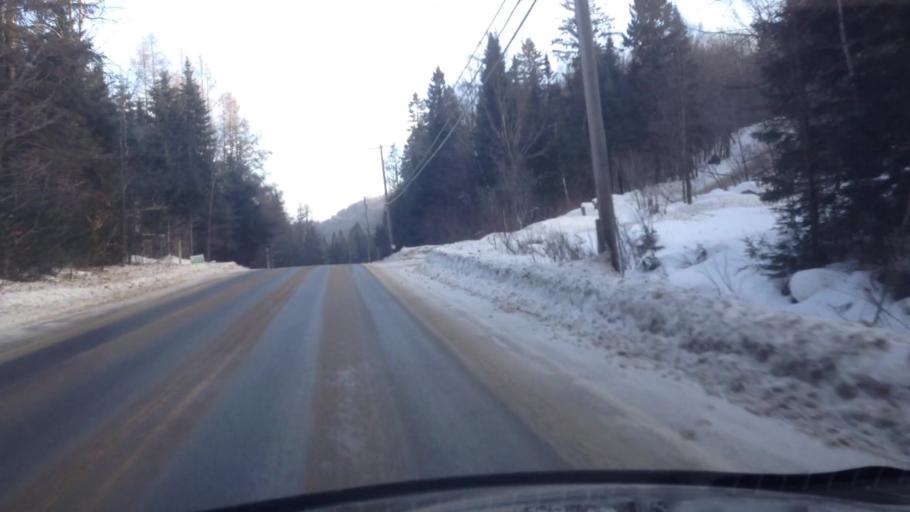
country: CA
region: Quebec
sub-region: Laurentides
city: Sainte-Agathe-des-Monts
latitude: 45.9195
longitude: -74.3790
